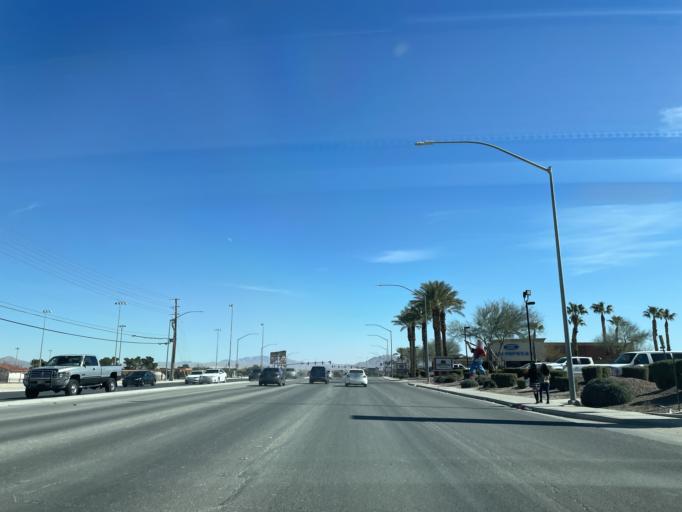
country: US
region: Nevada
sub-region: Clark County
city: North Las Vegas
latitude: 36.2393
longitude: -115.1560
